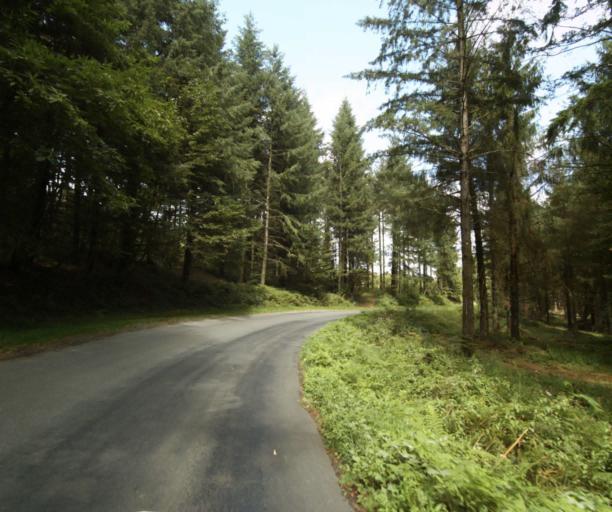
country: FR
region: Limousin
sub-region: Departement de la Correze
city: Sainte-Fortunade
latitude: 45.1931
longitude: 1.8145
